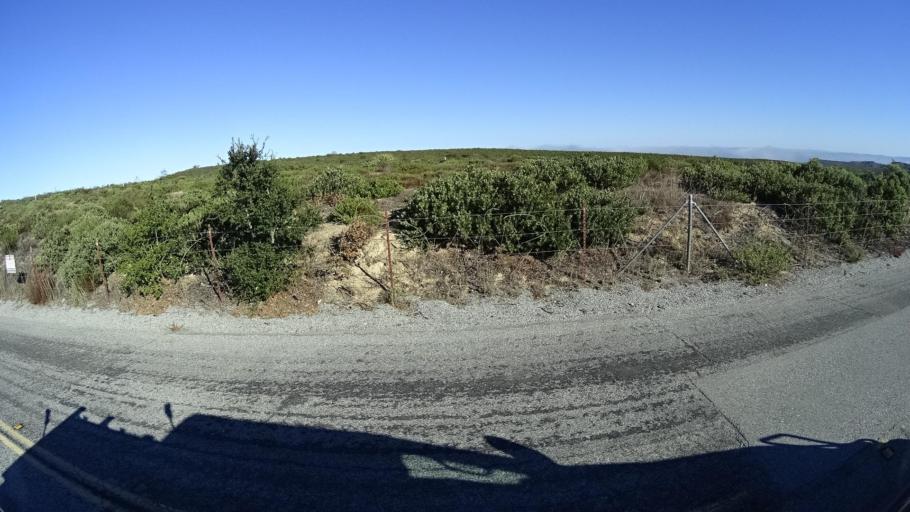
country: US
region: California
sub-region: Monterey County
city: Del Rey Oaks
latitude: 36.5868
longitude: -121.7702
